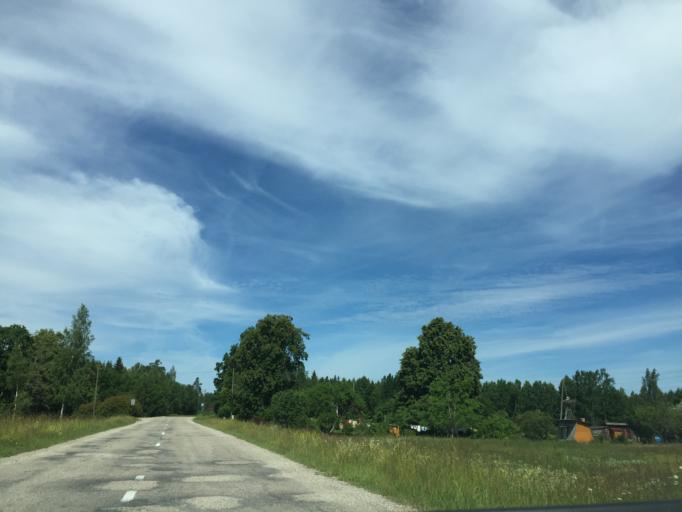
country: LV
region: Dundaga
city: Dundaga
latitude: 57.5595
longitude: 22.3169
